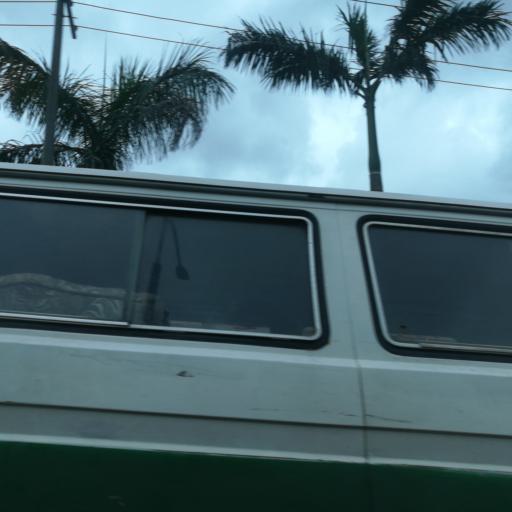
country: NG
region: Lagos
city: Ikoyi
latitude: 6.4630
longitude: 3.4258
